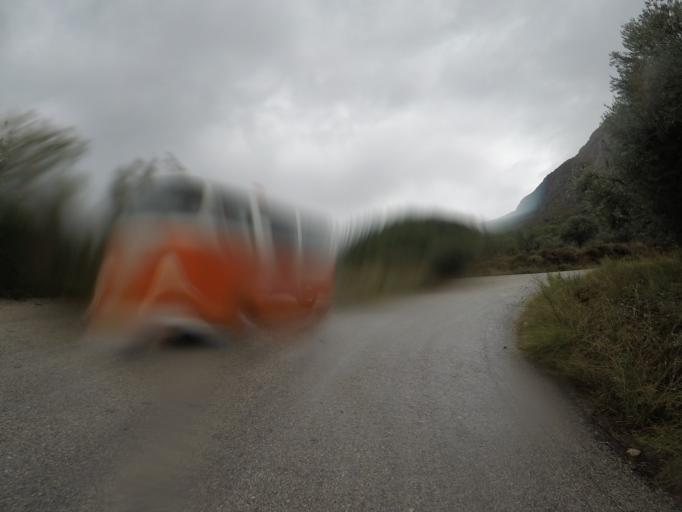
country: GR
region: Peloponnese
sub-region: Nomos Korinthias
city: Arkhaia Korinthos
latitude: 37.8991
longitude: 22.8821
